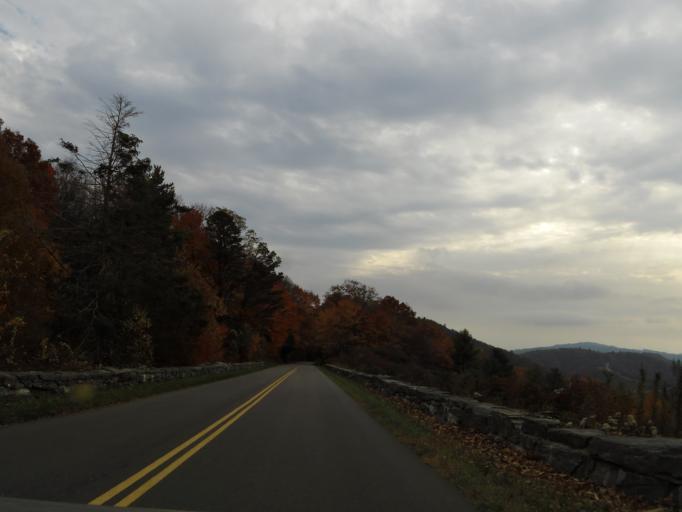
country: US
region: North Carolina
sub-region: Alleghany County
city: Sparta
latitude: 36.4285
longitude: -81.1840
